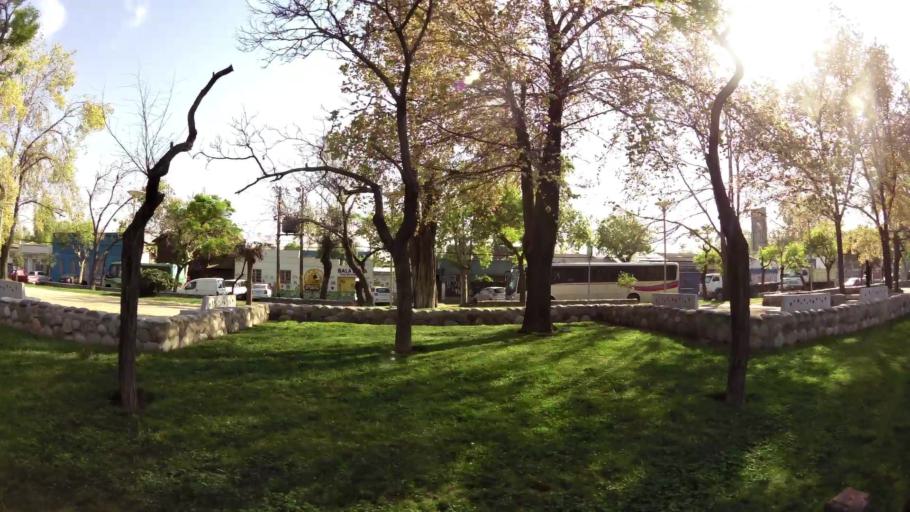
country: CL
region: Santiago Metropolitan
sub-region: Provincia de Maipo
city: San Bernardo
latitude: -33.5901
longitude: -70.7035
